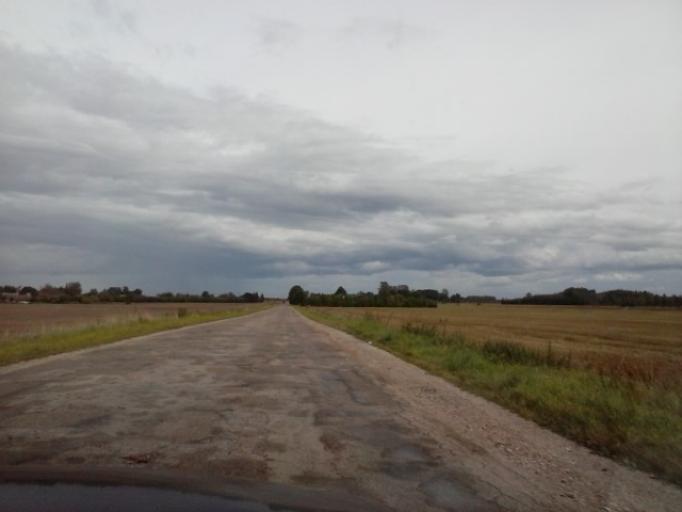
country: LV
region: Tukuma Rajons
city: Tukums
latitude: 56.9219
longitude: 23.2268
